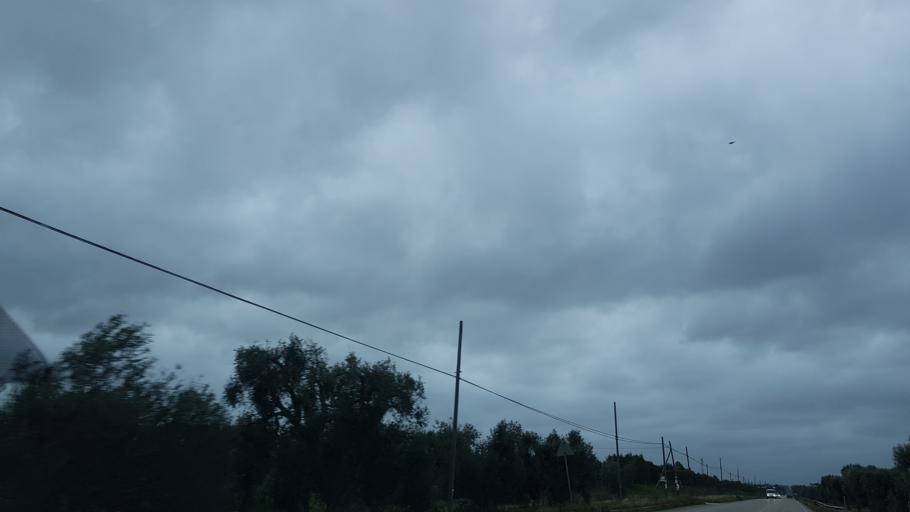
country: IT
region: Apulia
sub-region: Provincia di Brindisi
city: San Vito dei Normanni
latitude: 40.6526
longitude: 17.7979
